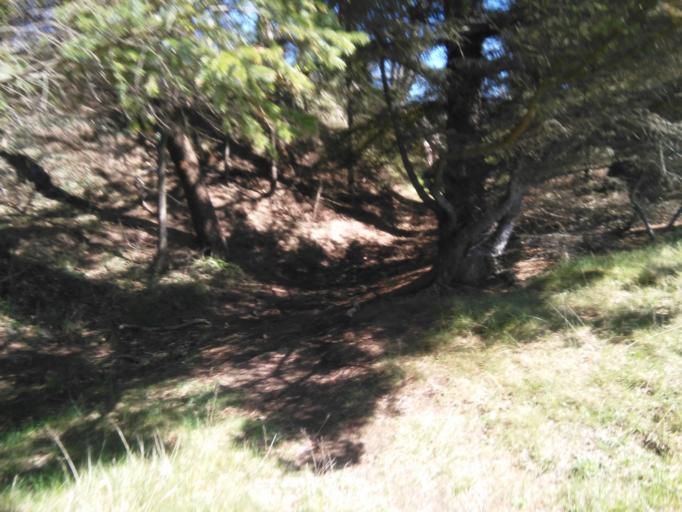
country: DK
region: Central Jutland
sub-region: Hedensted Kommune
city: Juelsminde
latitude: 55.7454
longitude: 10.0806
